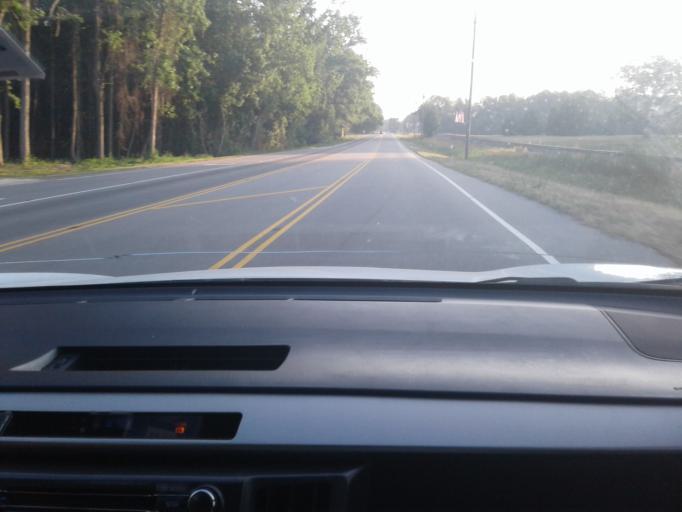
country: US
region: North Carolina
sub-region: Harnett County
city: Lillington
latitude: 35.4796
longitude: -78.8206
